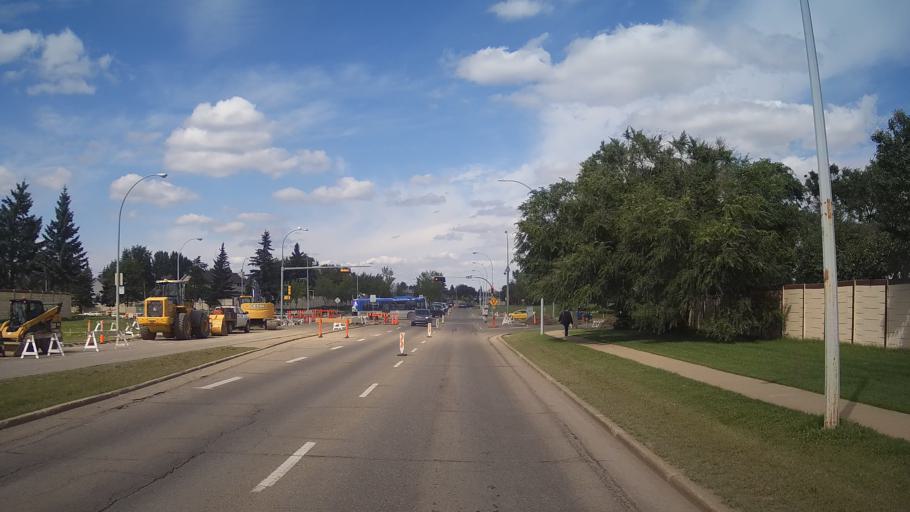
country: CA
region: Alberta
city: St. Albert
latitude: 53.5274
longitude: -113.6299
